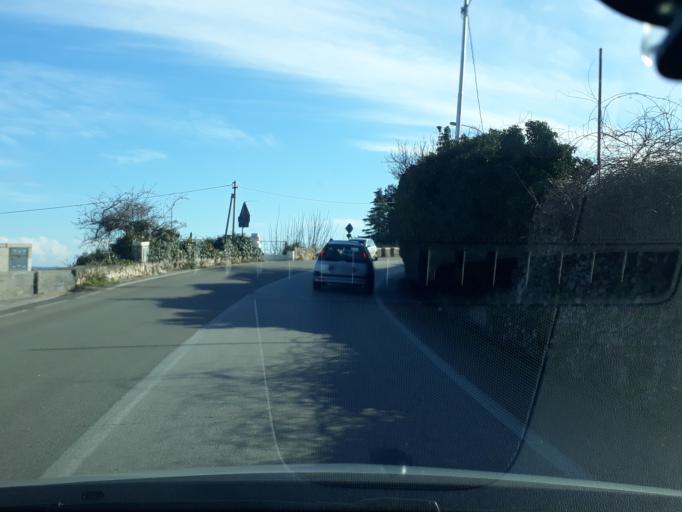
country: IT
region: Apulia
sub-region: Provincia di Taranto
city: Martina Franca
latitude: 40.7091
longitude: 17.3368
